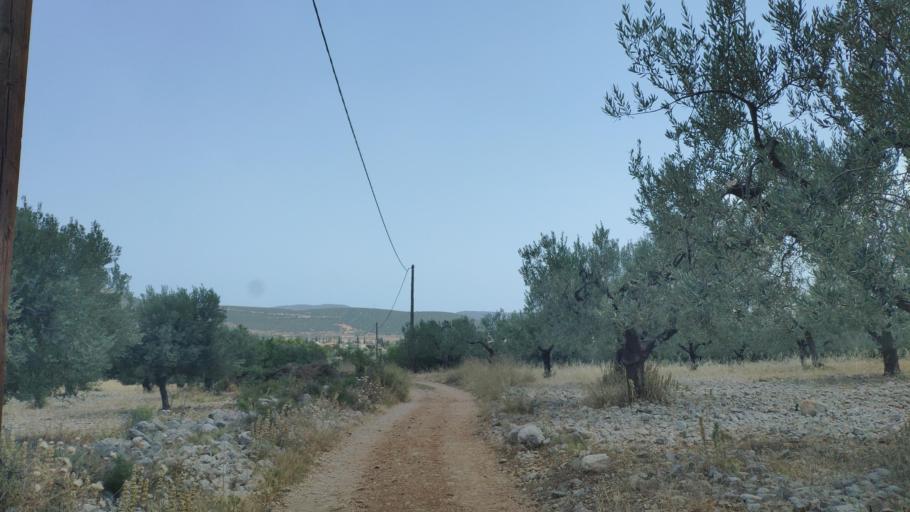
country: GR
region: Peloponnese
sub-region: Nomos Argolidos
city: Didyma
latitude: 37.4713
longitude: 23.1650
